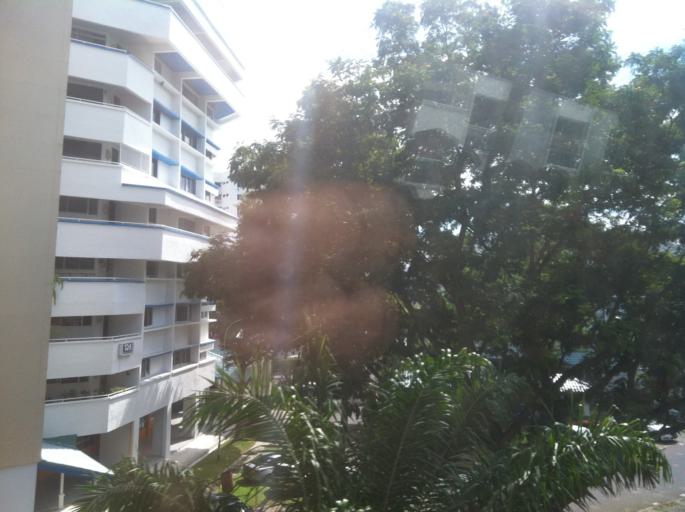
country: SG
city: Singapore
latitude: 1.3173
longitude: 103.8871
